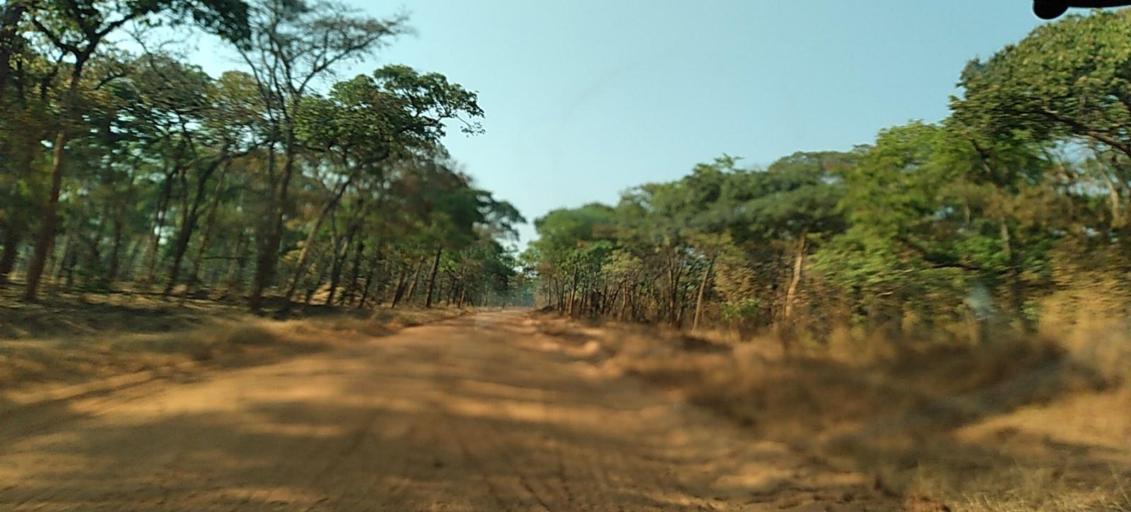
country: ZM
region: North-Western
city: Kasempa
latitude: -13.6079
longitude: 25.9778
